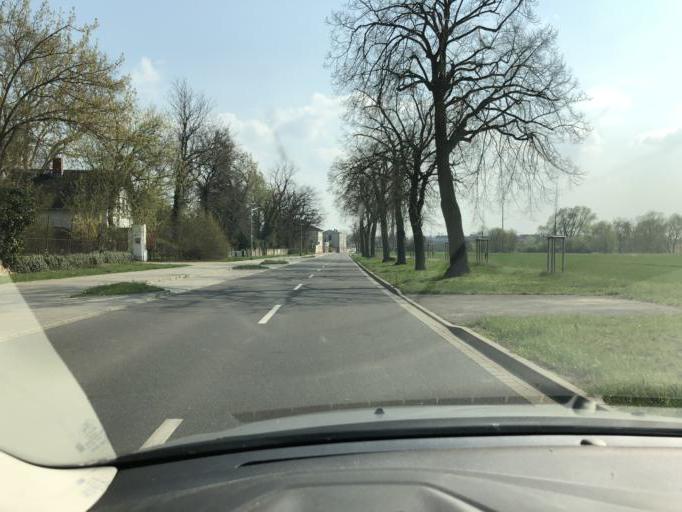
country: DE
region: Saxony-Anhalt
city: Grobers
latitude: 51.4386
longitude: 12.1170
